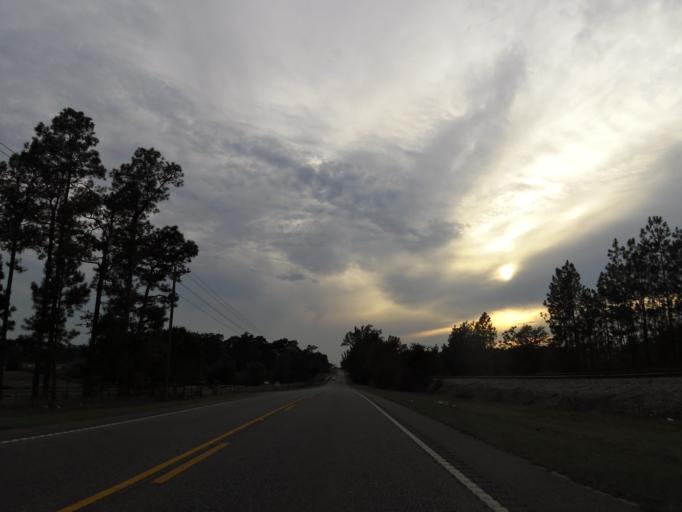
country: US
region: Alabama
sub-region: Escambia County
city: Atmore
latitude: 31.0144
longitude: -87.5564
